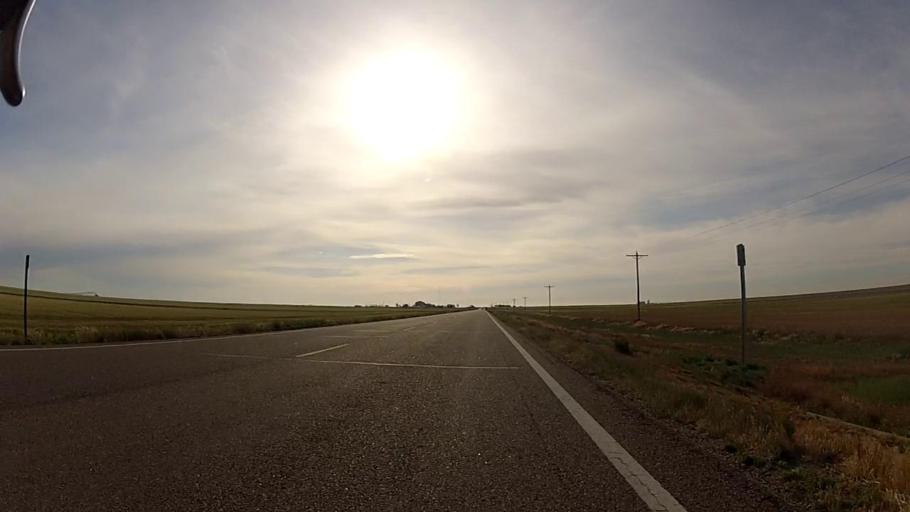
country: US
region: Kansas
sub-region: Grant County
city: Ulysses
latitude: 37.5767
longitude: -101.4987
